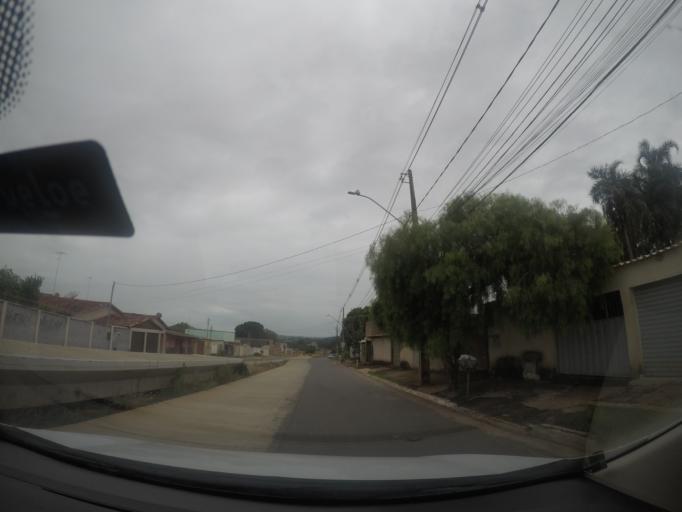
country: BR
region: Goias
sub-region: Goiania
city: Goiania
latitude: -16.6176
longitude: -49.2988
